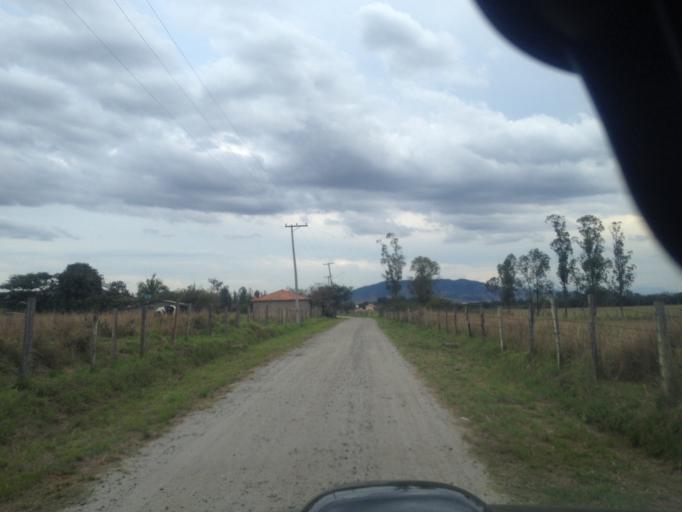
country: BR
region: Rio de Janeiro
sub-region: Porto Real
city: Porto Real
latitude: -22.4122
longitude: -44.2764
